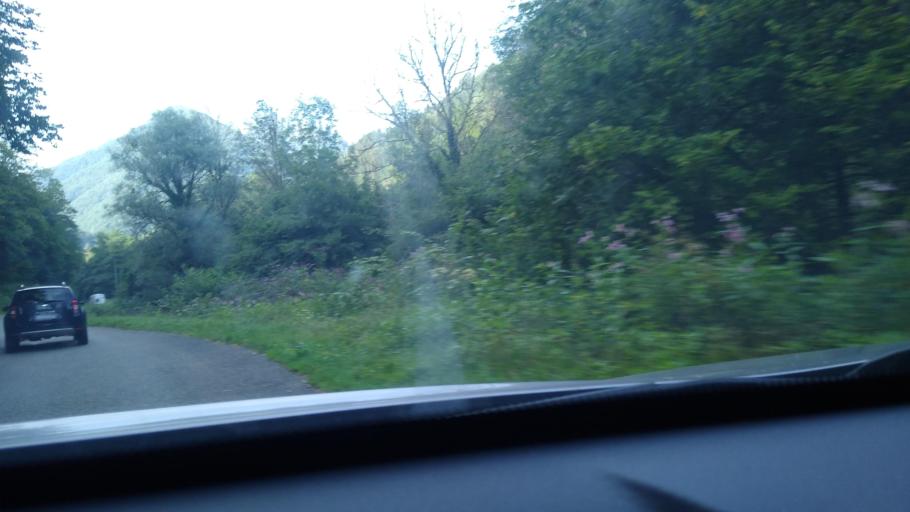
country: FR
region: Midi-Pyrenees
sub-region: Departement de l'Ariege
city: Saint-Girons
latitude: 42.8007
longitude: 1.1928
